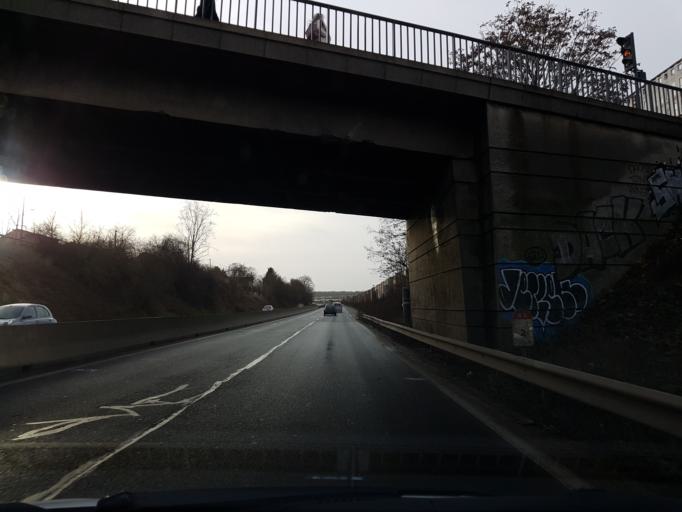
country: FR
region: Ile-de-France
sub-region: Departement de l'Essonne
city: Montgeron
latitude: 48.7040
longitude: 2.4436
